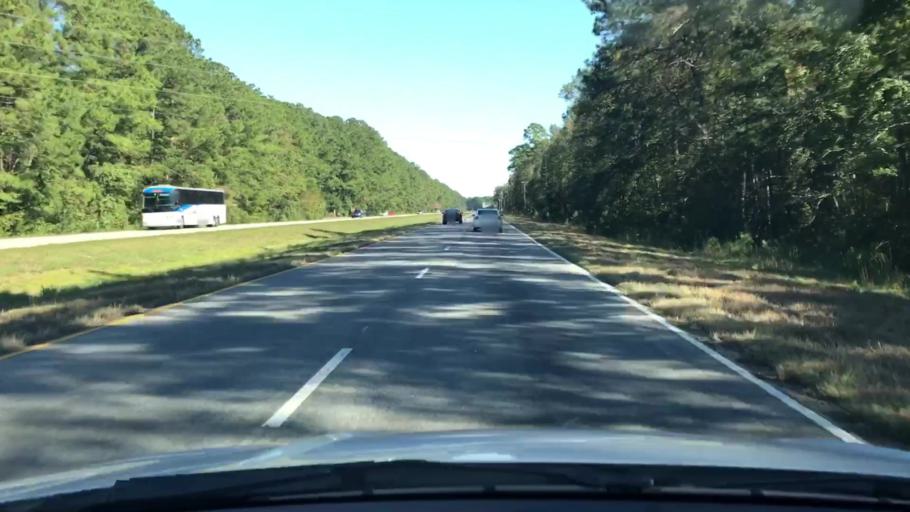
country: US
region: South Carolina
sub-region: Charleston County
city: Ravenel
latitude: 32.7818
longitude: -80.1951
